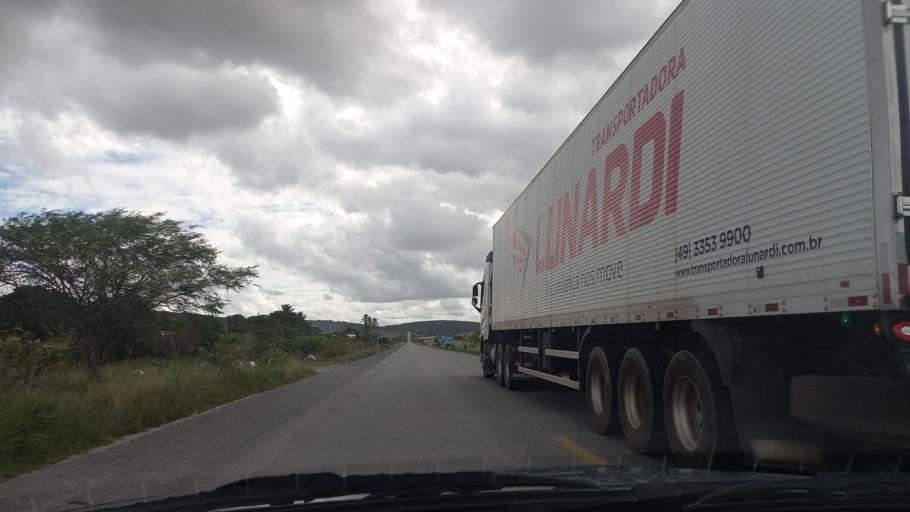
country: BR
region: Pernambuco
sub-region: Lajedo
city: Lajedo
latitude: -8.6679
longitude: -36.3723
